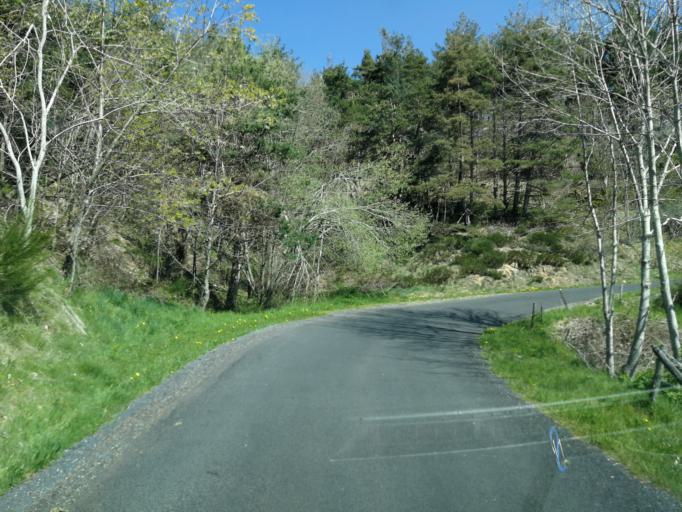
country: FR
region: Rhone-Alpes
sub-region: Departement de l'Ardeche
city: Le Cheylard
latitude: 44.9377
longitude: 4.4248
